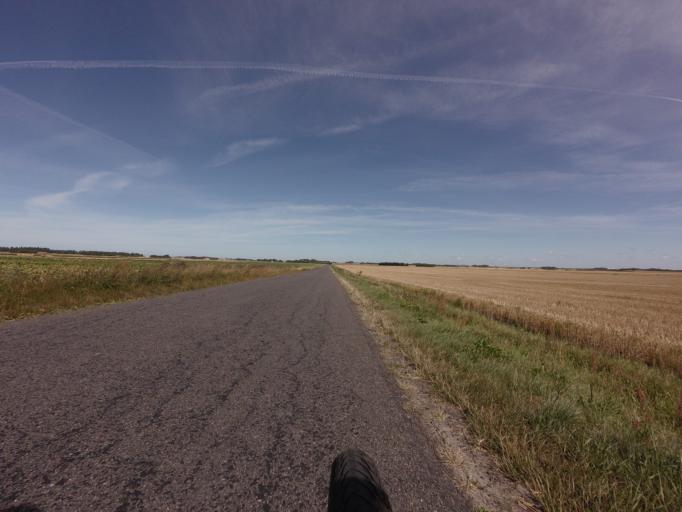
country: DK
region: North Denmark
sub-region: Bronderslev Kommune
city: Bronderslev
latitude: 57.3098
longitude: 9.8099
